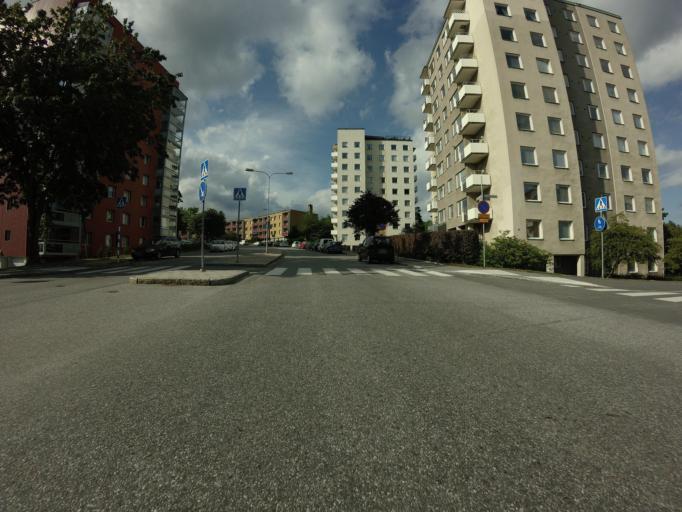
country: SE
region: Stockholm
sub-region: Lidingo
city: Lidingoe
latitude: 59.3725
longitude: 18.1475
